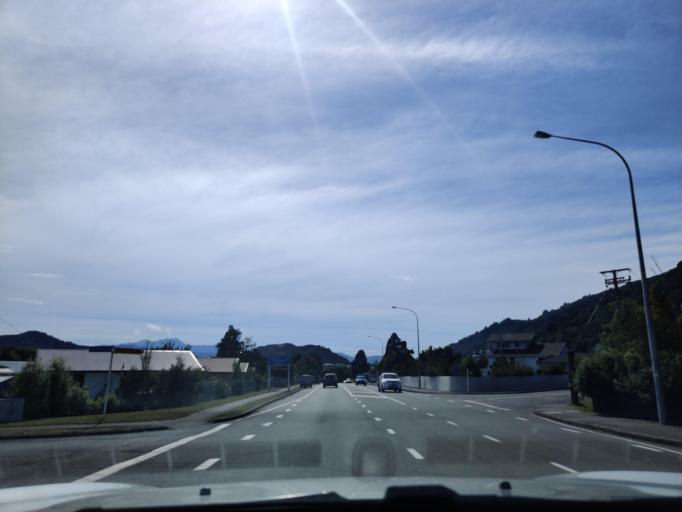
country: NZ
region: Marlborough
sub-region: Marlborough District
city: Picton
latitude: -41.2984
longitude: 173.9996
